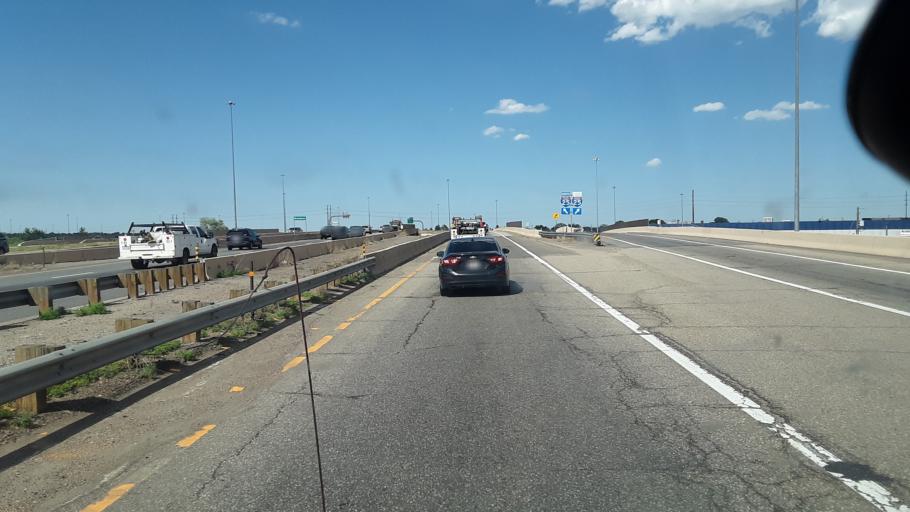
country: US
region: Colorado
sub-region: Adams County
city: Twin Lakes
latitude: 39.8139
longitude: -104.9889
